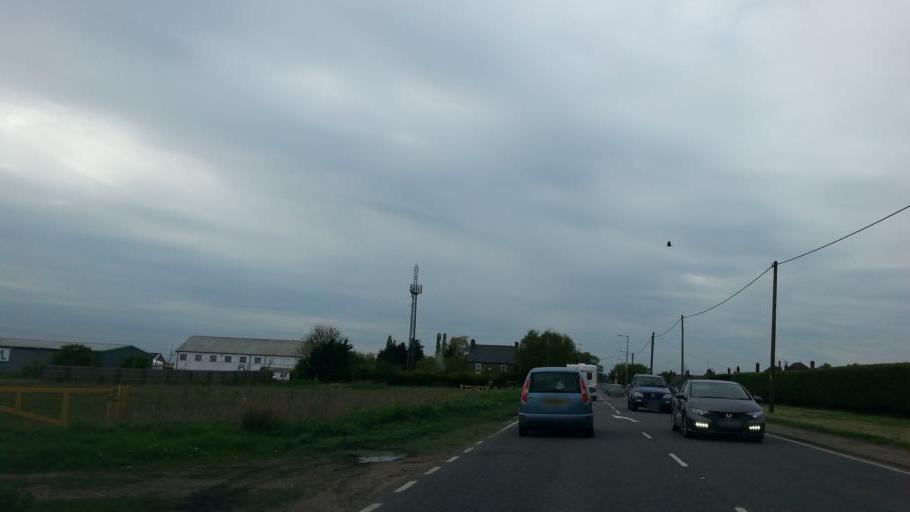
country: GB
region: England
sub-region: Cambridgeshire
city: March
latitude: 52.5664
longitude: 0.0620
